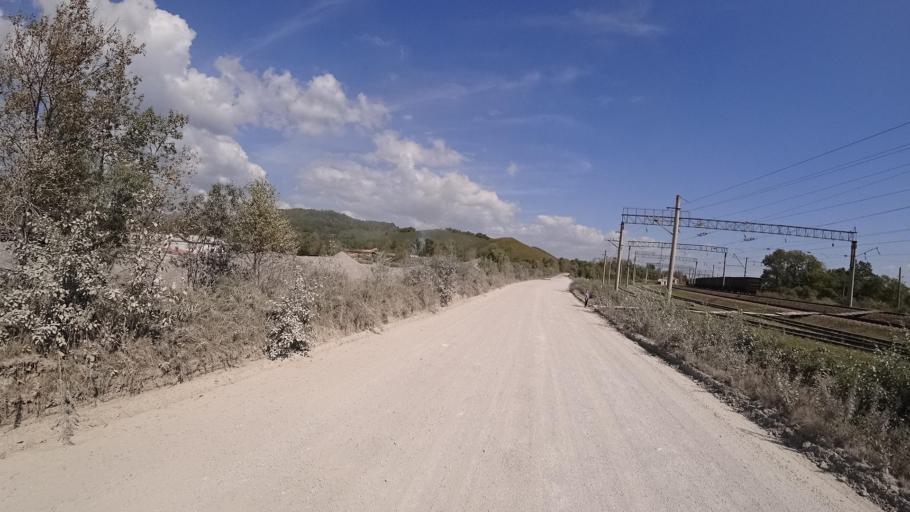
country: RU
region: Jewish Autonomous Oblast
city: Londoko
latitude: 49.0072
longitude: 131.9380
